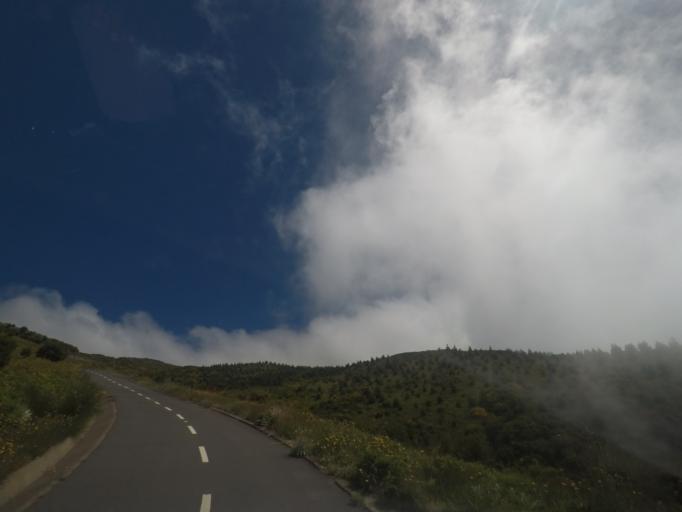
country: PT
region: Madeira
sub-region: Camara de Lobos
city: Curral das Freiras
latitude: 32.7073
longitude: -16.9391
